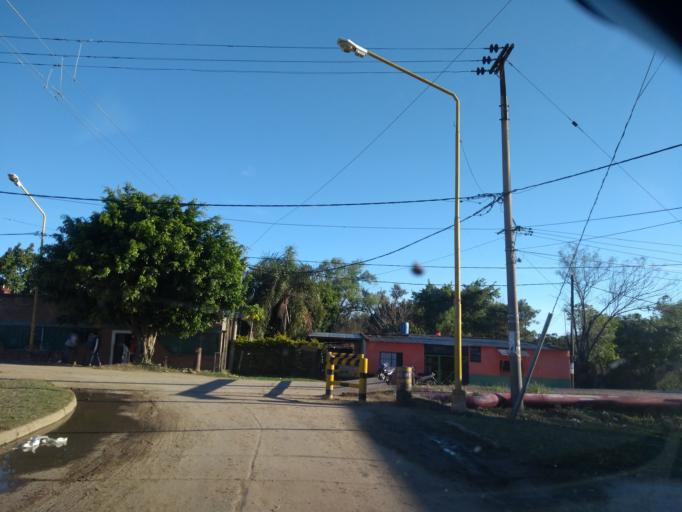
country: AR
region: Chaco
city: Puerto Vilelas
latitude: -27.5009
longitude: -58.9340
